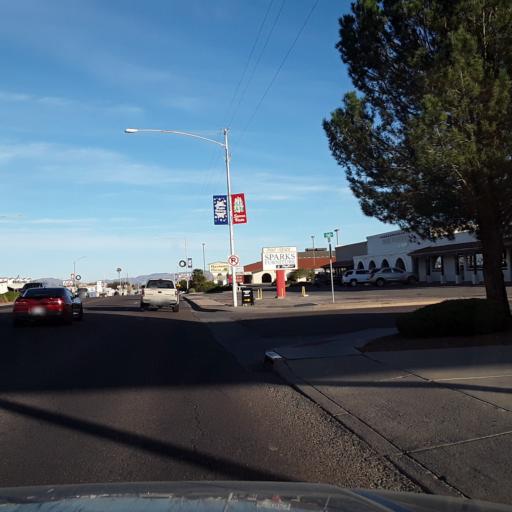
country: US
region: Arizona
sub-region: Cochise County
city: Sierra Vista
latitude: 31.5545
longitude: -110.2970
